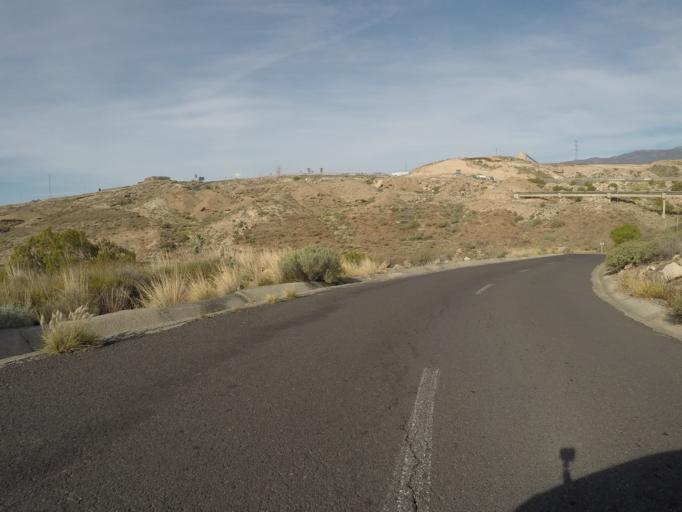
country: ES
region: Canary Islands
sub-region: Provincia de Santa Cruz de Tenerife
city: Lomo de Arico
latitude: 28.1182
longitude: -16.4723
